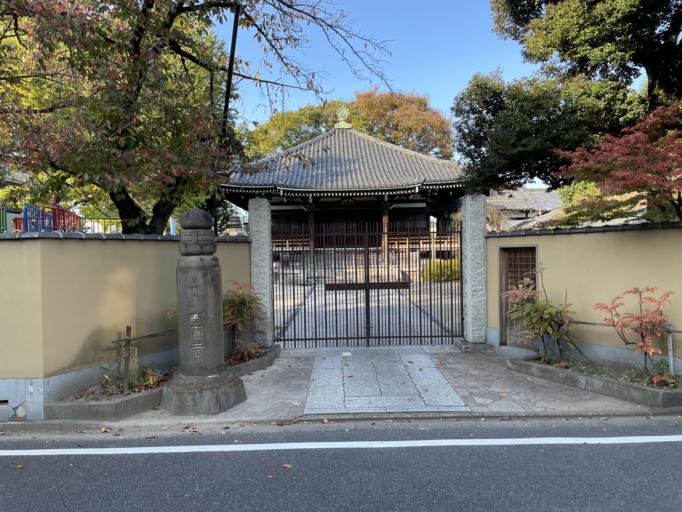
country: JP
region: Chiba
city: Matsudo
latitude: 35.7385
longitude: 139.8514
